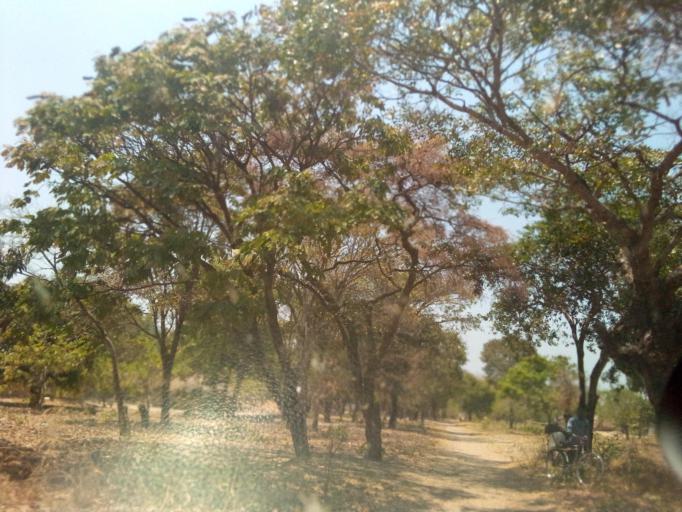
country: ZM
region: Copperbelt
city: Kataba
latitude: -12.2552
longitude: 30.3581
